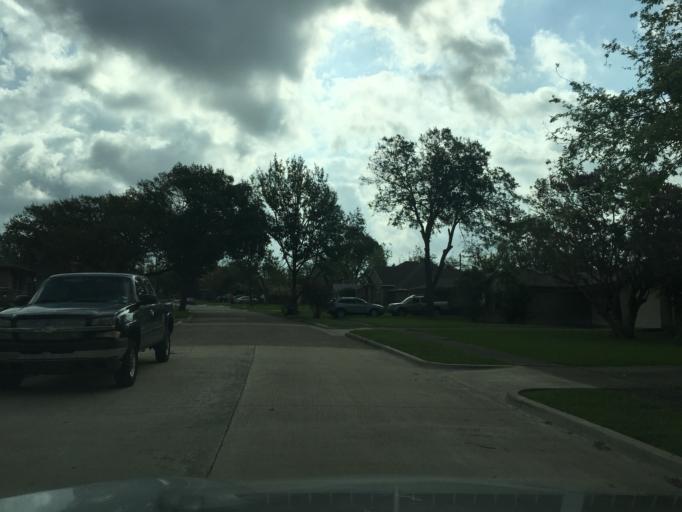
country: US
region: Texas
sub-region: Dallas County
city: Richardson
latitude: 32.8991
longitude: -96.7553
